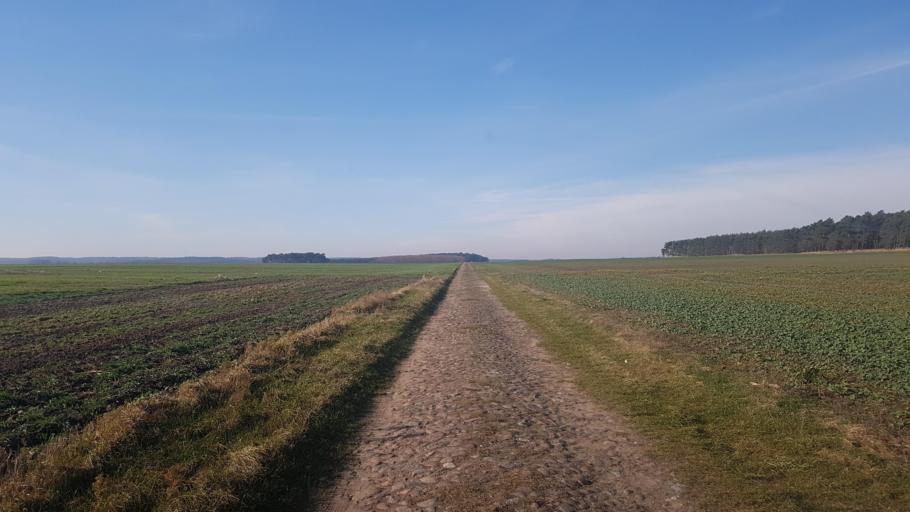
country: DE
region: Brandenburg
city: Niemegk
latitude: 52.1189
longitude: 12.6689
